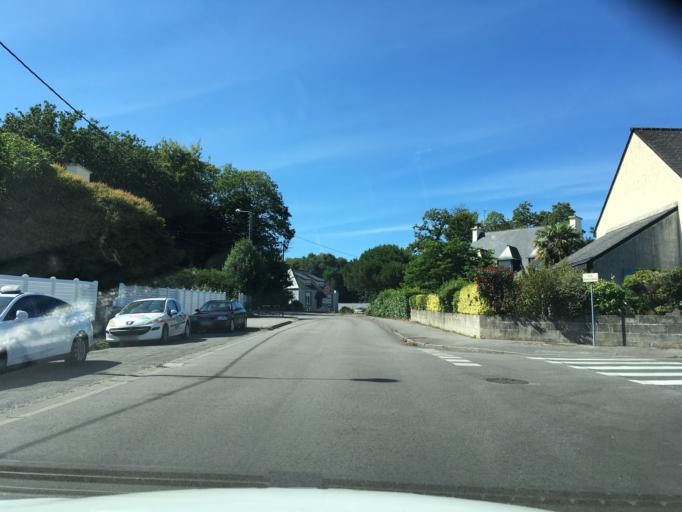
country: FR
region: Brittany
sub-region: Departement du Finistere
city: Quimper
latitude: 47.9726
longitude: -4.1262
